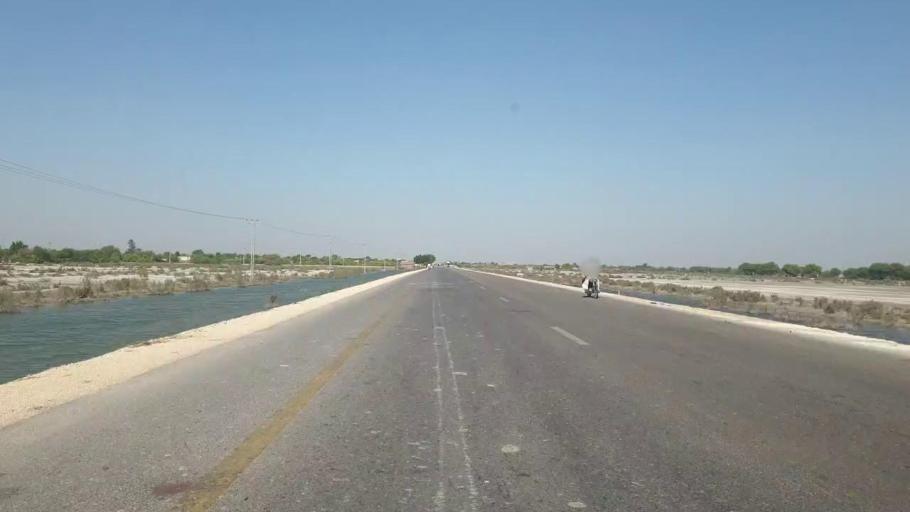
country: PK
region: Sindh
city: Talhar
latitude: 24.8440
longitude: 68.8163
